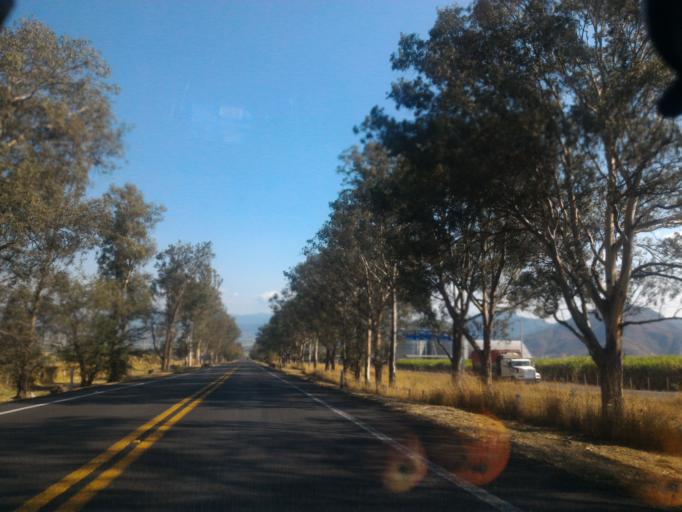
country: MX
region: Jalisco
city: Tuxpan
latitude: 19.5486
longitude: -103.4326
